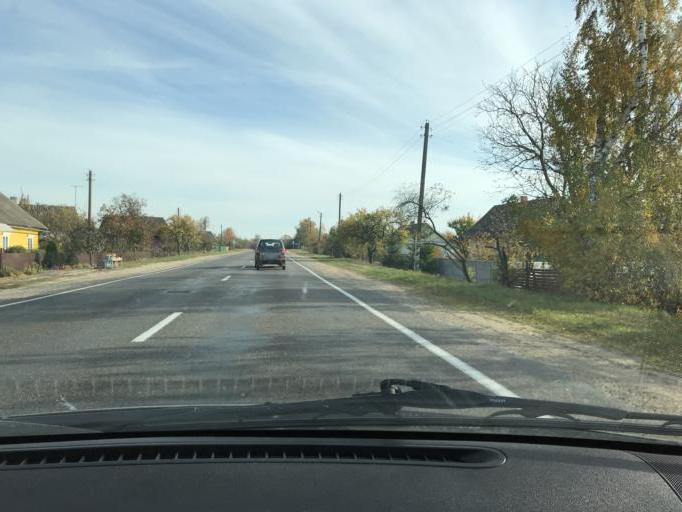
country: BY
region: Brest
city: Lahishyn
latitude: 52.2367
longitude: 26.0091
